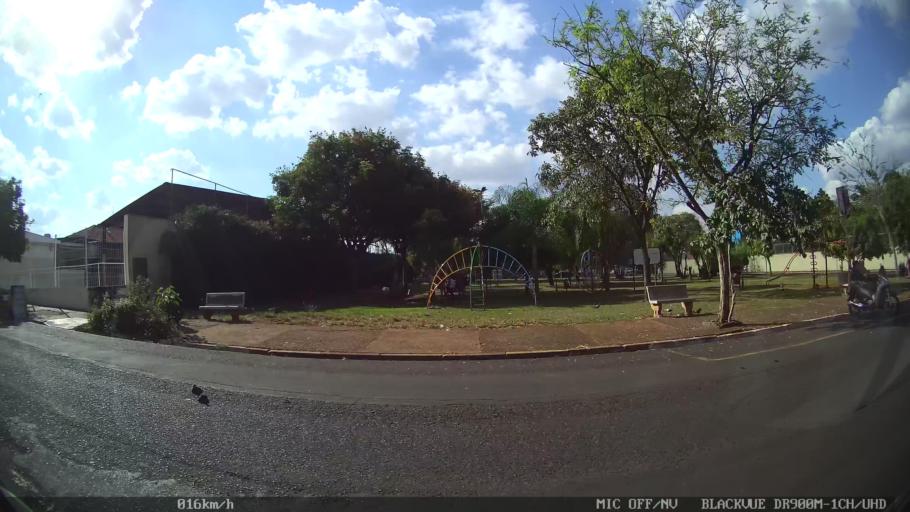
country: BR
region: Sao Paulo
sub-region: Ribeirao Preto
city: Ribeirao Preto
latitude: -21.1893
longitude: -47.8277
